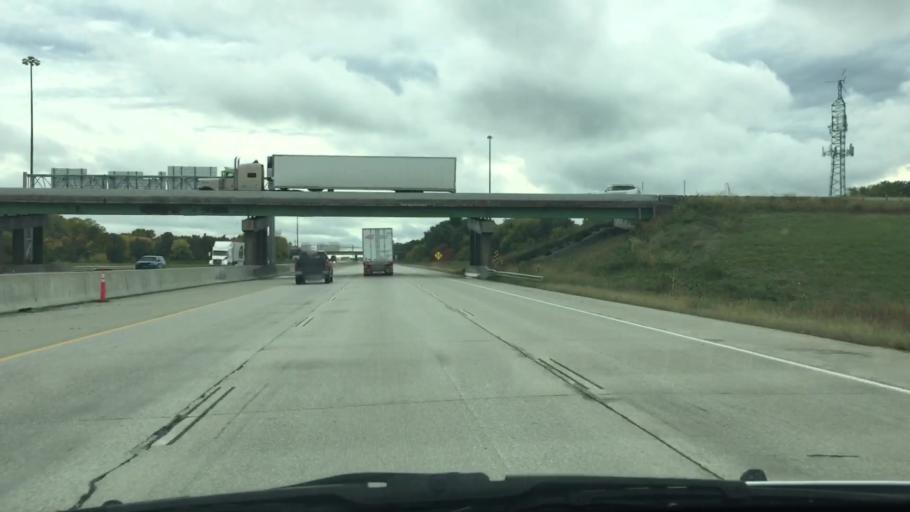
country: US
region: Iowa
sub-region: Polk County
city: Clive
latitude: 41.5901
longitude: -93.7776
